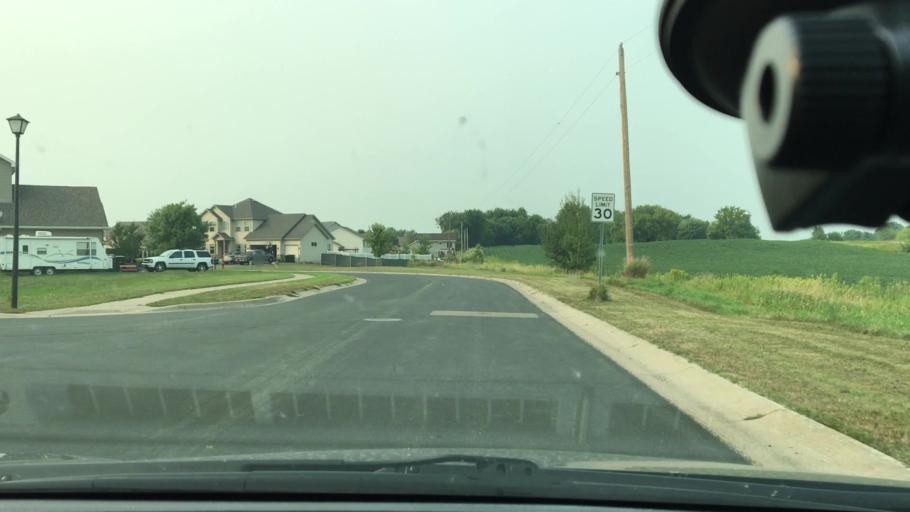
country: US
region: Minnesota
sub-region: Wright County
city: Albertville
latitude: 45.2531
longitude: -93.6531
